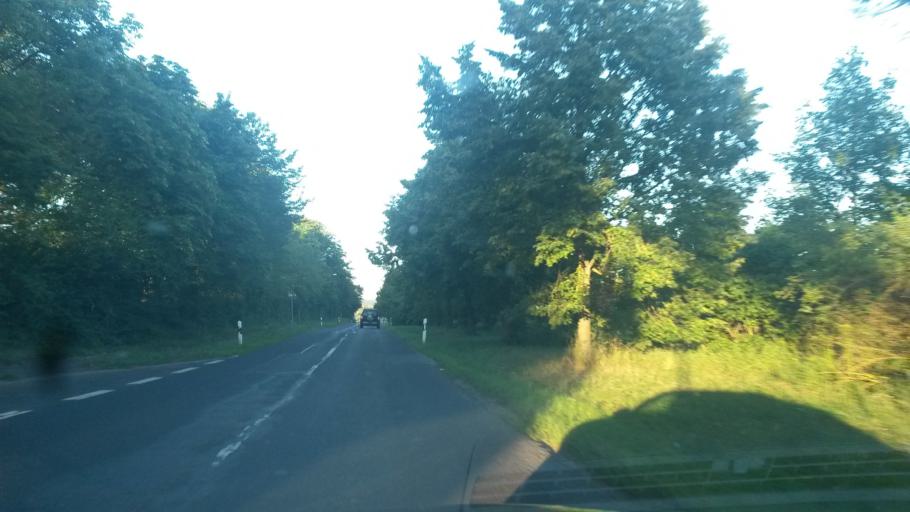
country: DE
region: Bavaria
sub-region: Regierungsbezirk Unterfranken
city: Wuerzburg
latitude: 49.8080
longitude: 9.9472
